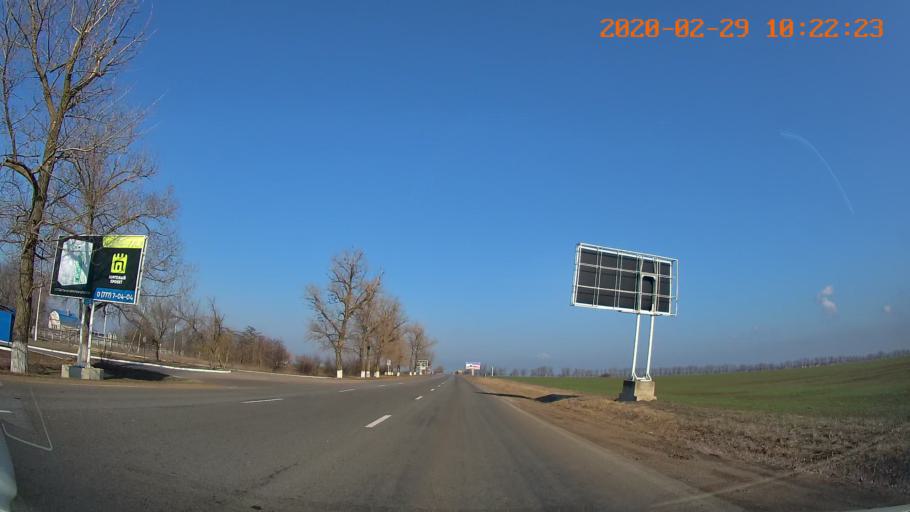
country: MD
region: Telenesti
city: Tiraspolul Nou
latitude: 46.8752
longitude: 29.6070
